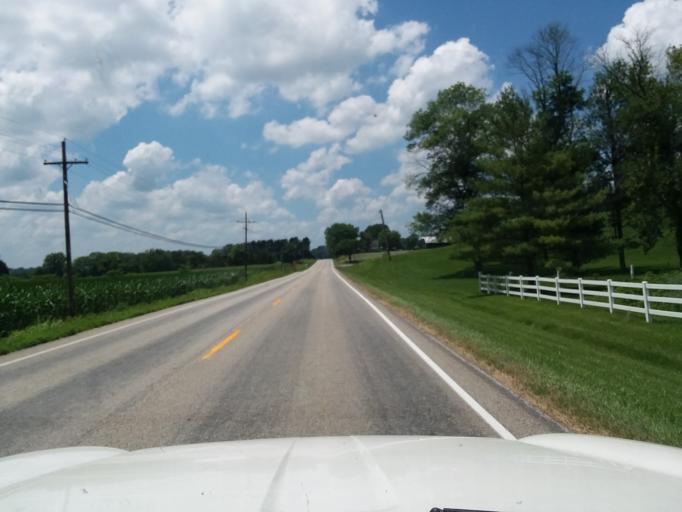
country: US
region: Indiana
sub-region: Johnson County
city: Trafalgar
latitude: 39.3717
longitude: -86.2873
